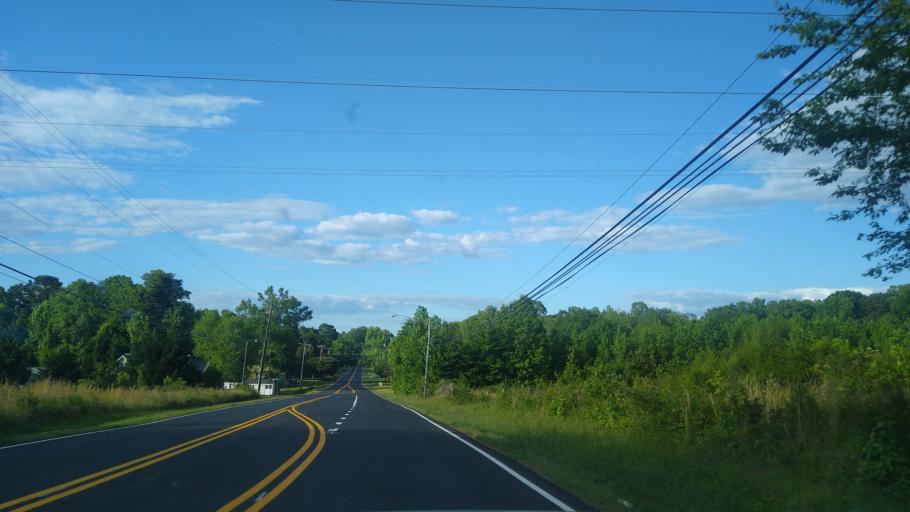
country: US
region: North Carolina
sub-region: Guilford County
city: McLeansville
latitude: 36.1637
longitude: -79.7312
